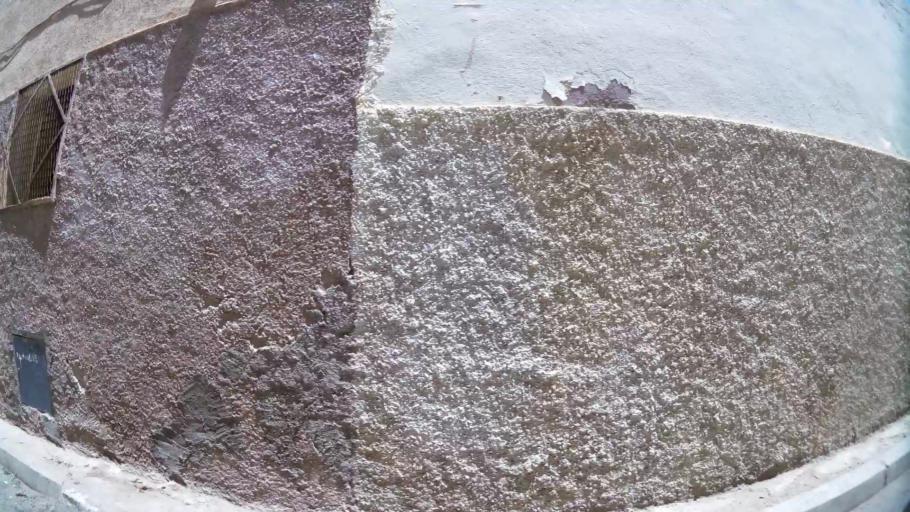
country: MA
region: Oriental
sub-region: Oujda-Angad
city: Oujda
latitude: 34.6729
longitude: -1.9283
